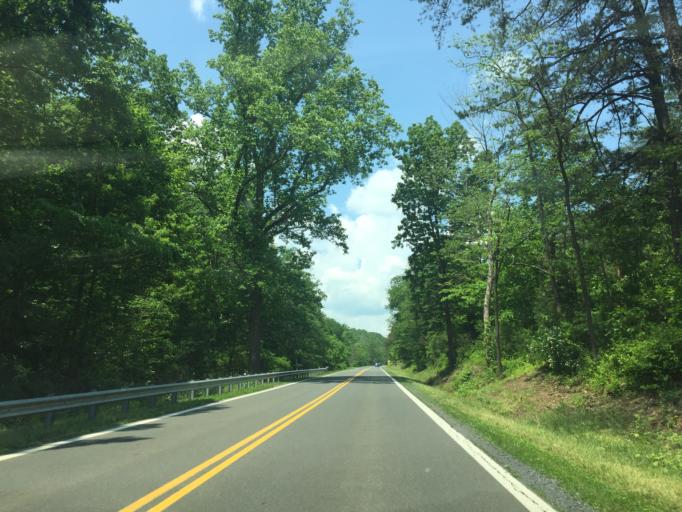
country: US
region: Virginia
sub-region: Shenandoah County
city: Strasburg
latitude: 39.0757
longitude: -78.3763
